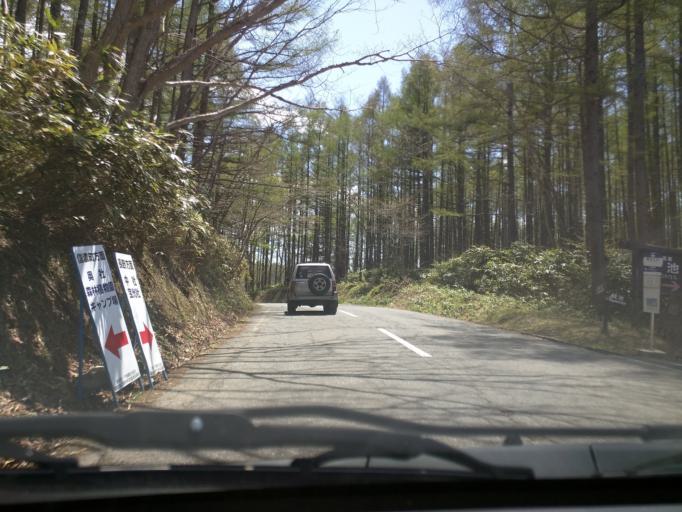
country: JP
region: Nagano
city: Nagano-shi
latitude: 36.7471
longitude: 138.0779
